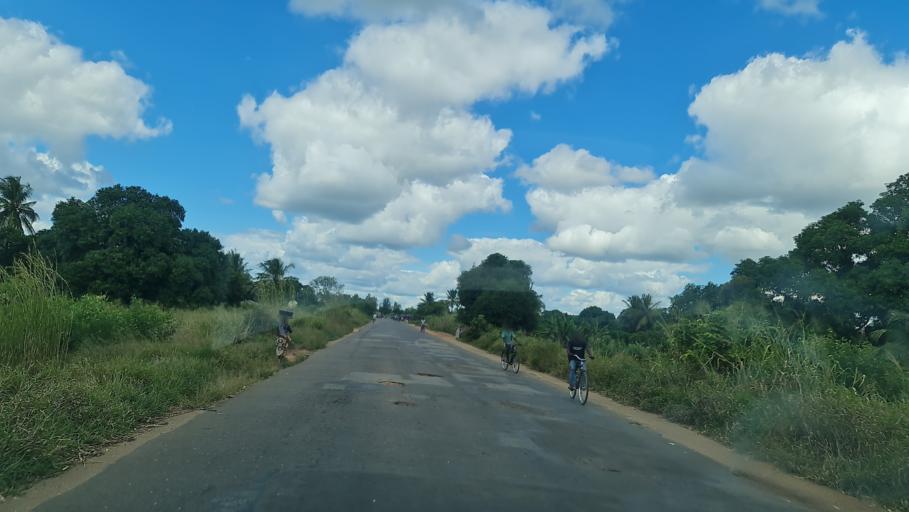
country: MZ
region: Zambezia
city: Quelimane
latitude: -17.5190
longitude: 36.2635
